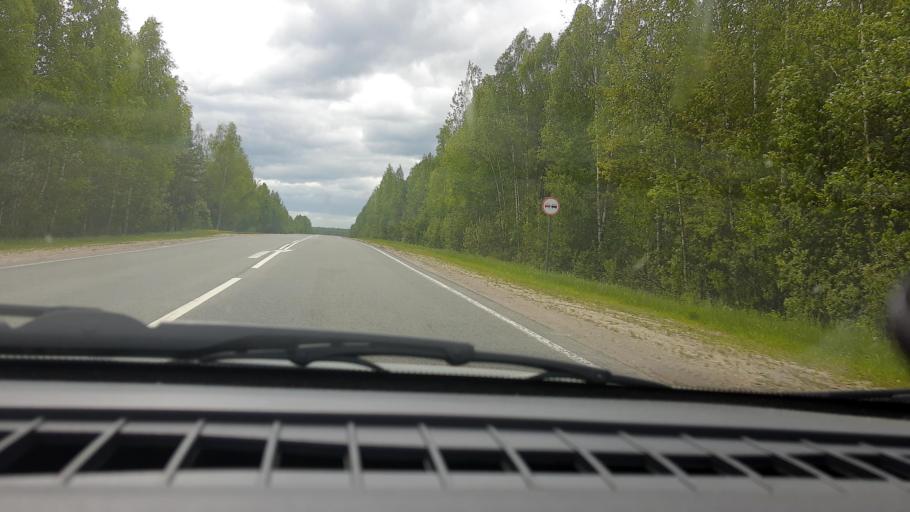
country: RU
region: Nizjnij Novgorod
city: Semenov
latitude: 56.7791
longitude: 44.4309
